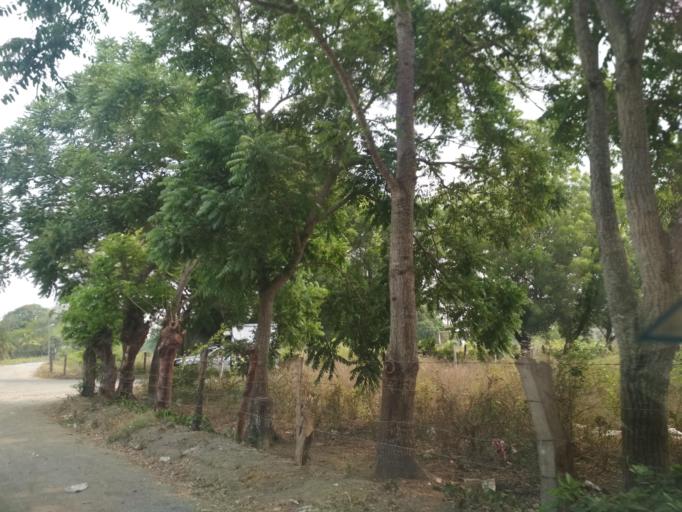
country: MX
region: Veracruz
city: Paso del Toro
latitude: 19.0215
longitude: -96.1505
